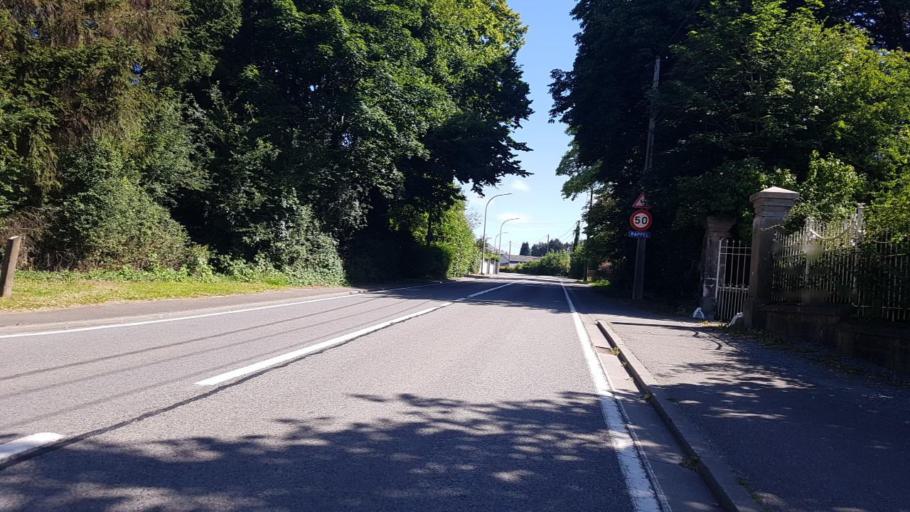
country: BE
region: Wallonia
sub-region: Province du Hainaut
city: Momignies
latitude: 50.0202
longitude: 4.1554
